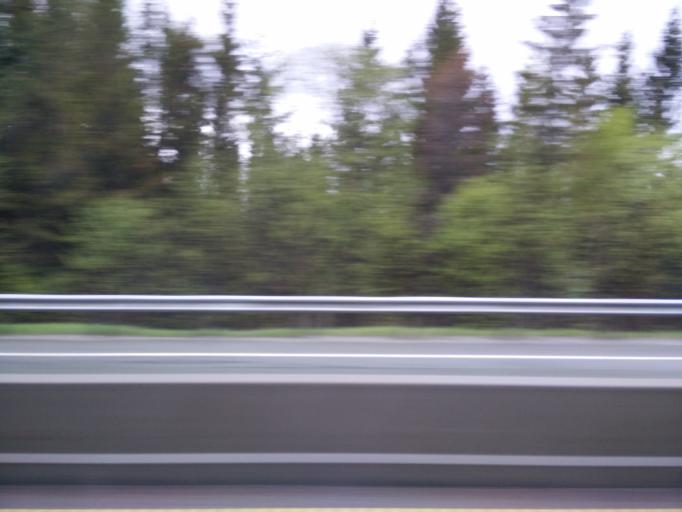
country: NO
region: Sor-Trondelag
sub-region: Malvik
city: Malvik
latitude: 63.4255
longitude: 10.7202
